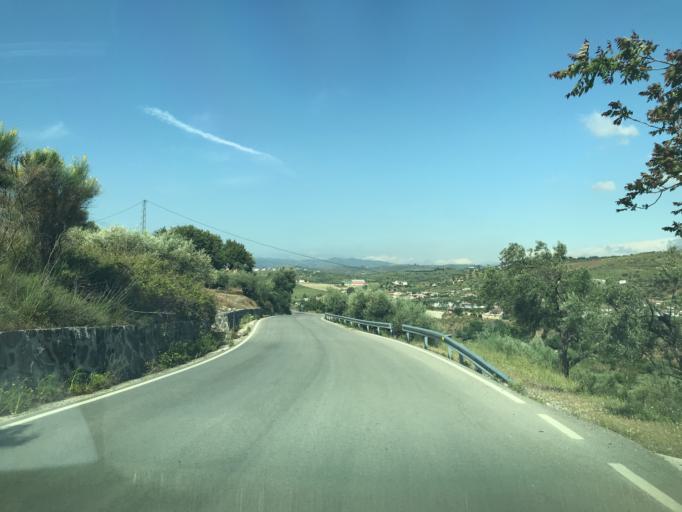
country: ES
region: Andalusia
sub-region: Provincia de Malaga
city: Alcaucin
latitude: 36.8942
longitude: -4.1327
